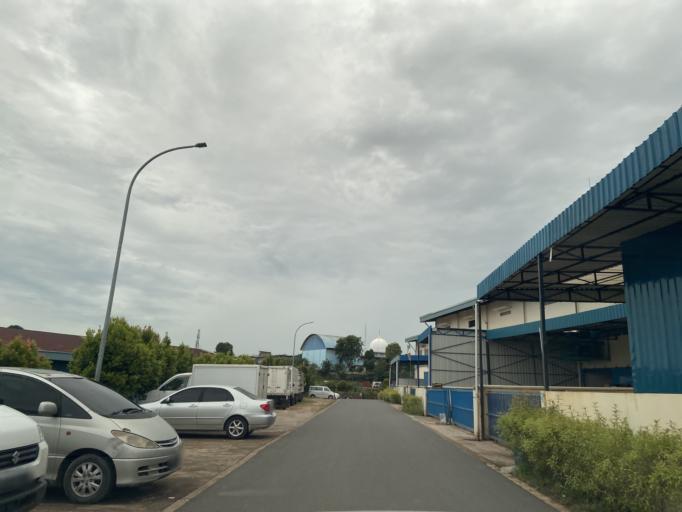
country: SG
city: Singapore
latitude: 1.1646
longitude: 104.0174
